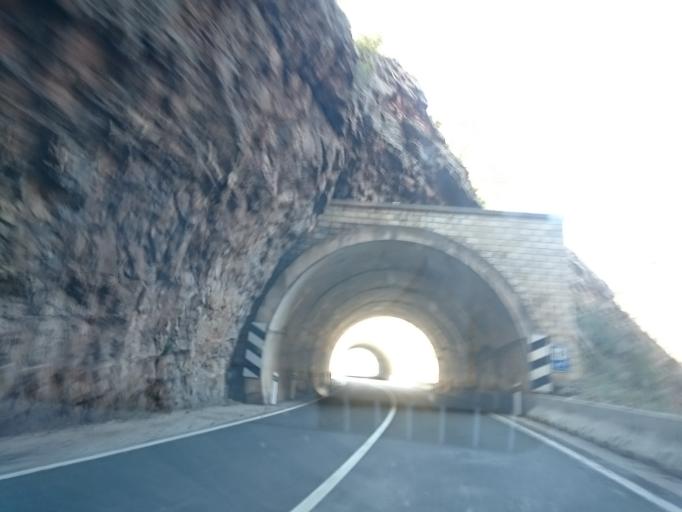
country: ES
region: Aragon
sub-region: Provincia de Huesca
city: Sopeira
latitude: 42.3242
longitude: 0.7422
